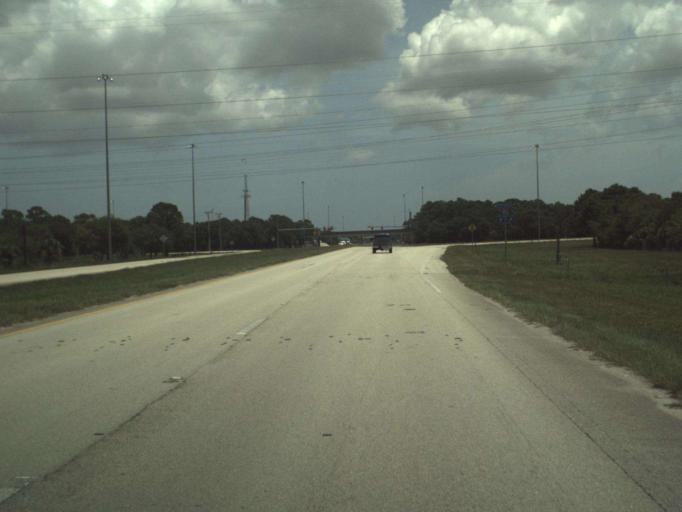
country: US
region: Florida
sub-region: Saint Lucie County
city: Fort Pierce South
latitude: 27.3744
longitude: -80.4155
